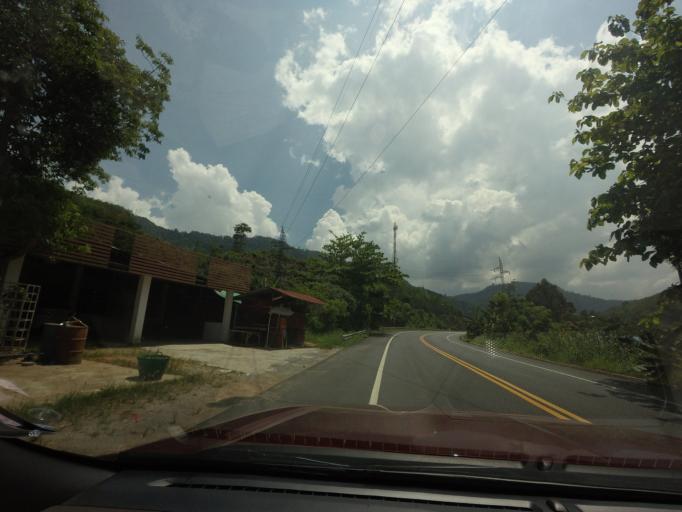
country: TH
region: Yala
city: Than To
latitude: 5.9817
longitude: 101.1994
